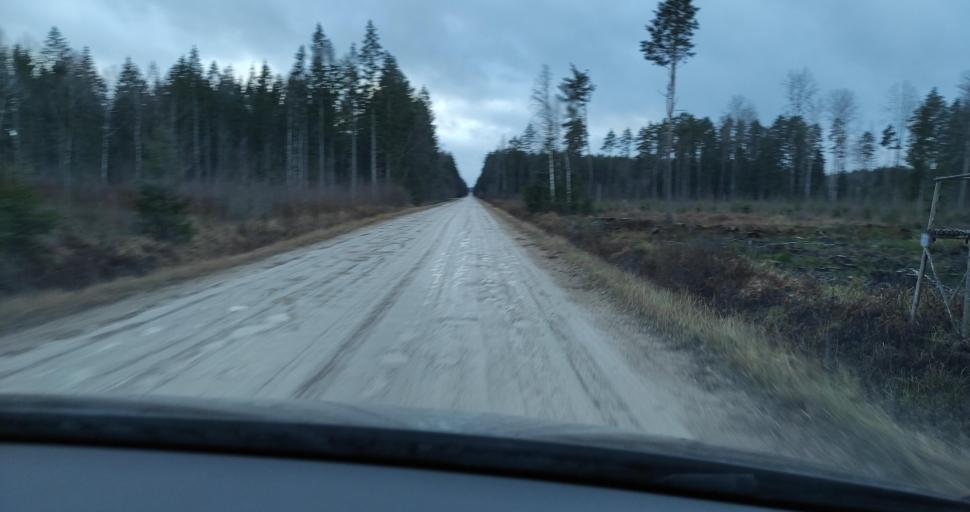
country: LV
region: Skrunda
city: Skrunda
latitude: 56.7393
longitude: 22.2050
